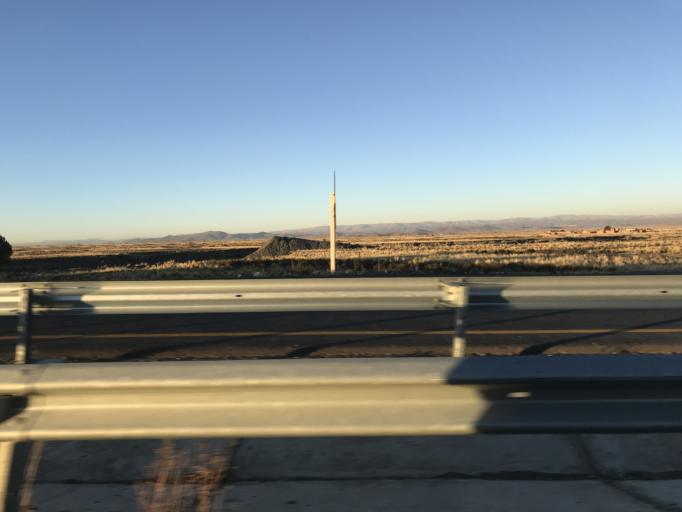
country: BO
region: La Paz
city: Batallas
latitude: -16.3112
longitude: -68.4546
